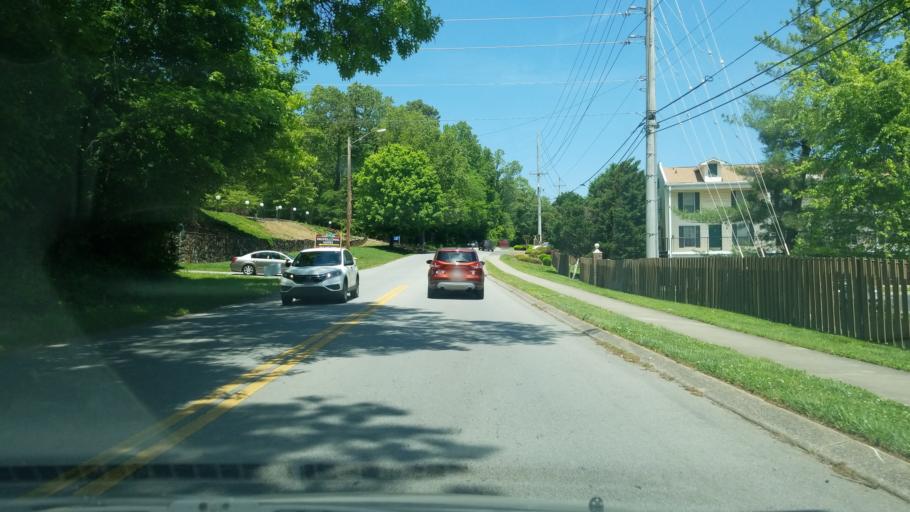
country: US
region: Tennessee
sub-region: Hamilton County
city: Signal Mountain
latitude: 35.1025
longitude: -85.3275
